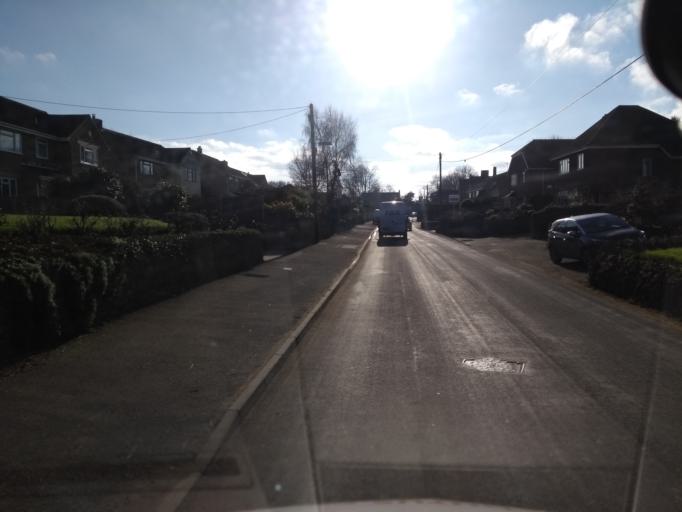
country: GB
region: England
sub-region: Somerset
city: South Petherton
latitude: 50.9462
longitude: -2.8041
